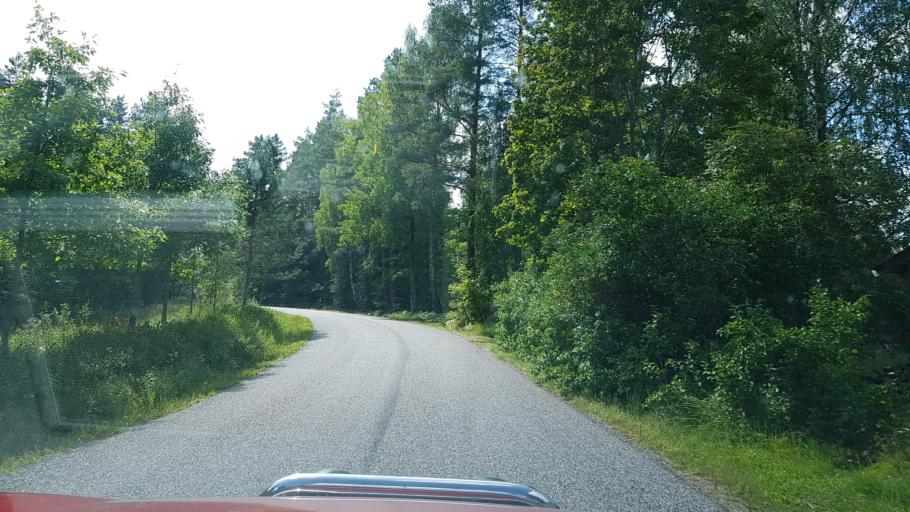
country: EE
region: Vorumaa
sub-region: Voru linn
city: Voru
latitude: 57.7155
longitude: 27.1966
